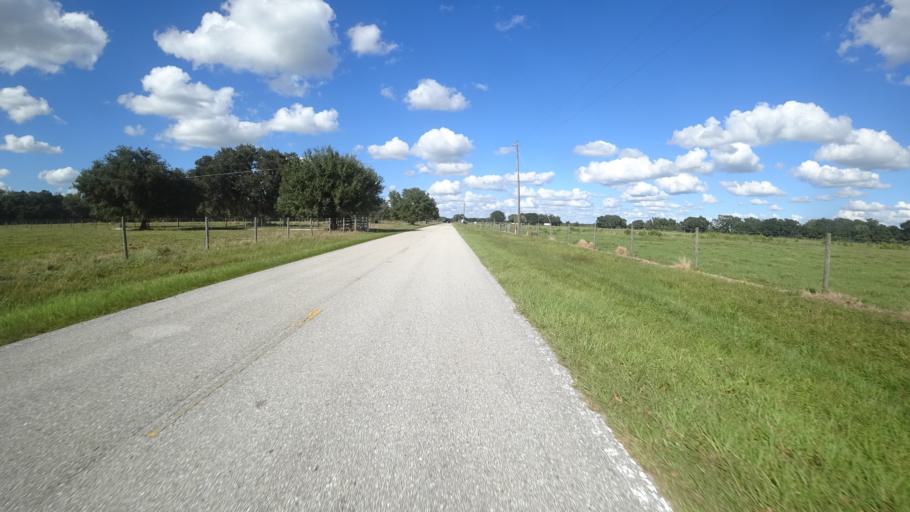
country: US
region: Florida
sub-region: Sarasota County
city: North Port
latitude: 27.2000
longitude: -82.1222
